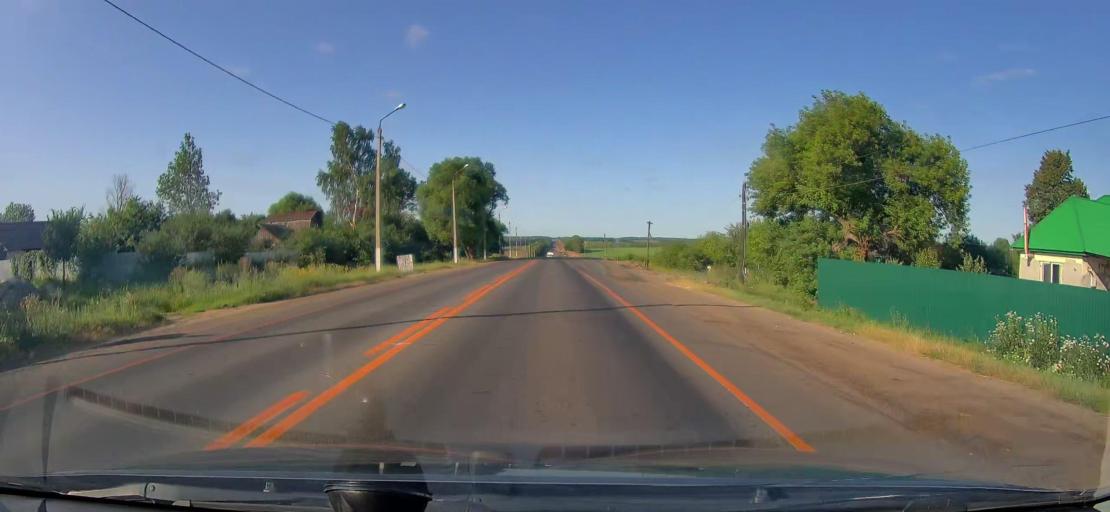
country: RU
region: Tula
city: Bol'shoye Skuratovo
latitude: 53.4281
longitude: 36.7957
